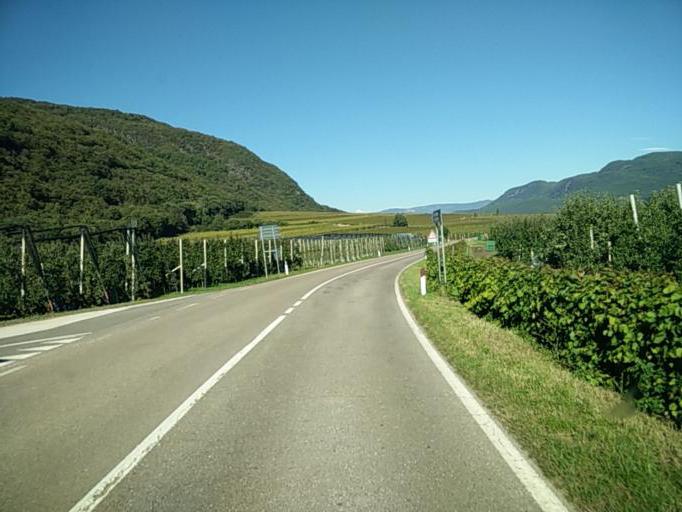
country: IT
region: Trentino-Alto Adige
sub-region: Bolzano
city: Termeno
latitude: 46.3547
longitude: 11.2493
